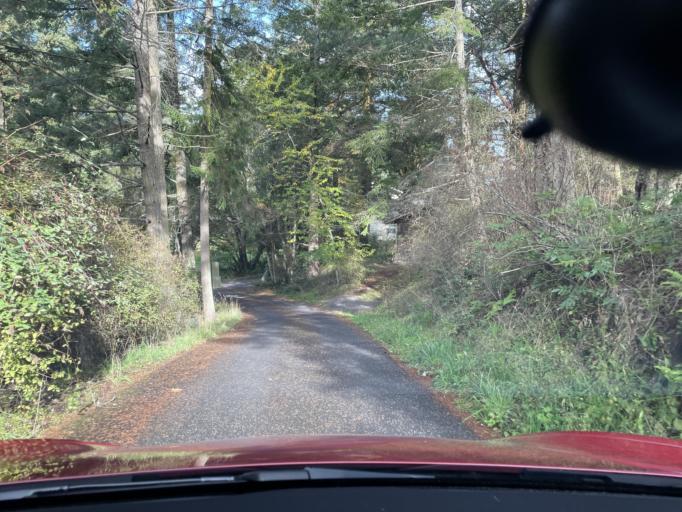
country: US
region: Washington
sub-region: San Juan County
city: Friday Harbor
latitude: 48.5331
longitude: -123.0293
